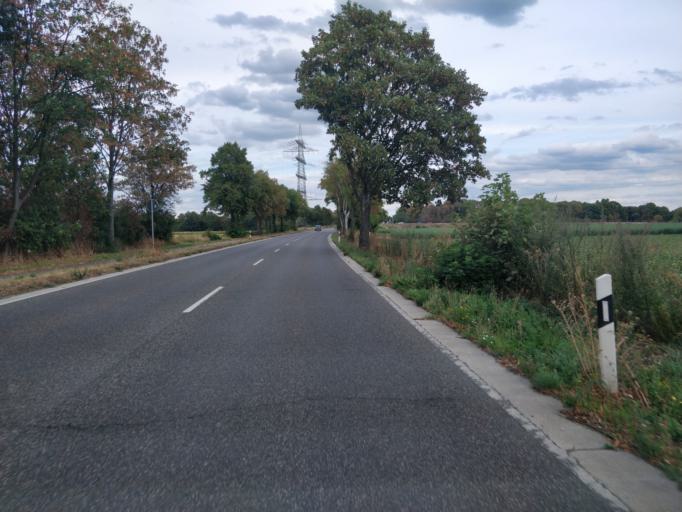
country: DE
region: North Rhine-Westphalia
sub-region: Regierungsbezirk Dusseldorf
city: Dormagen
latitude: 51.0920
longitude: 6.7972
